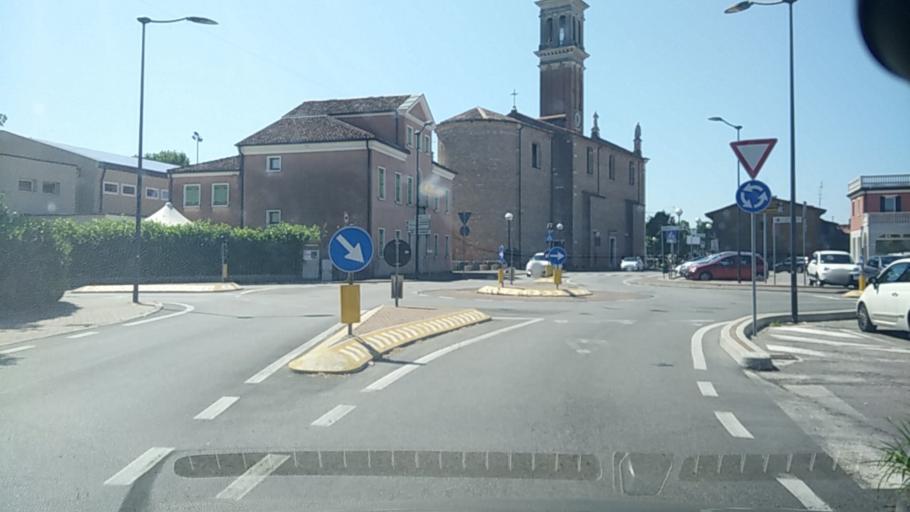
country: IT
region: Veneto
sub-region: Provincia di Venezia
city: Camponogara
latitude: 45.3865
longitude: 12.0721
